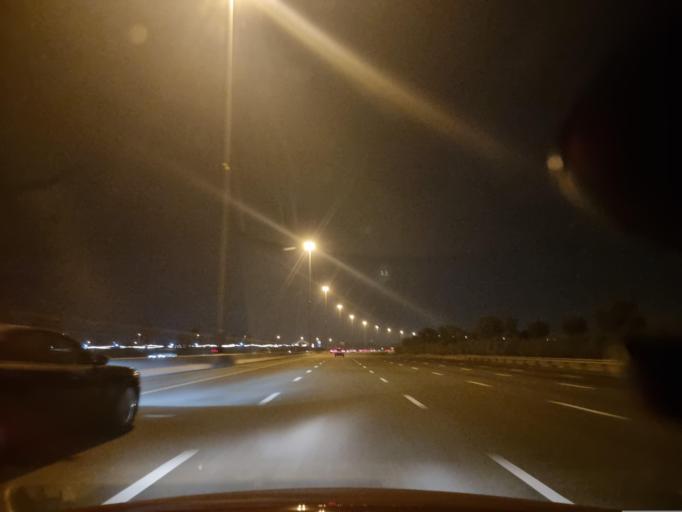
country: AE
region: Dubai
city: Dubai
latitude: 25.0658
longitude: 55.2942
